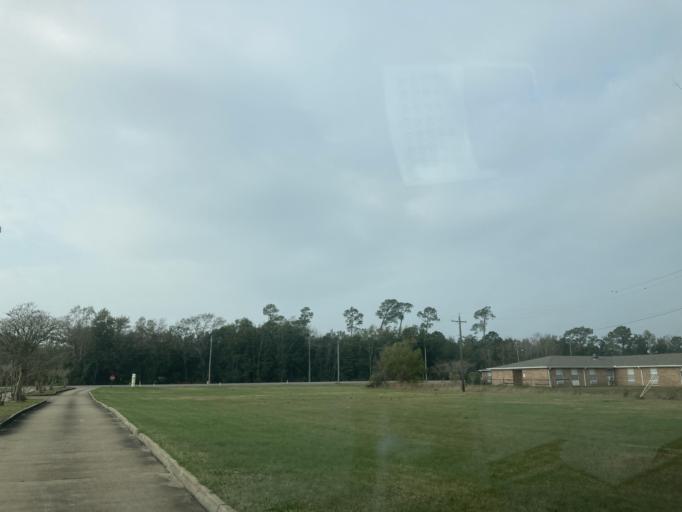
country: US
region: Mississippi
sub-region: Harrison County
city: Gulfport
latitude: 30.3695
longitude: -89.1177
